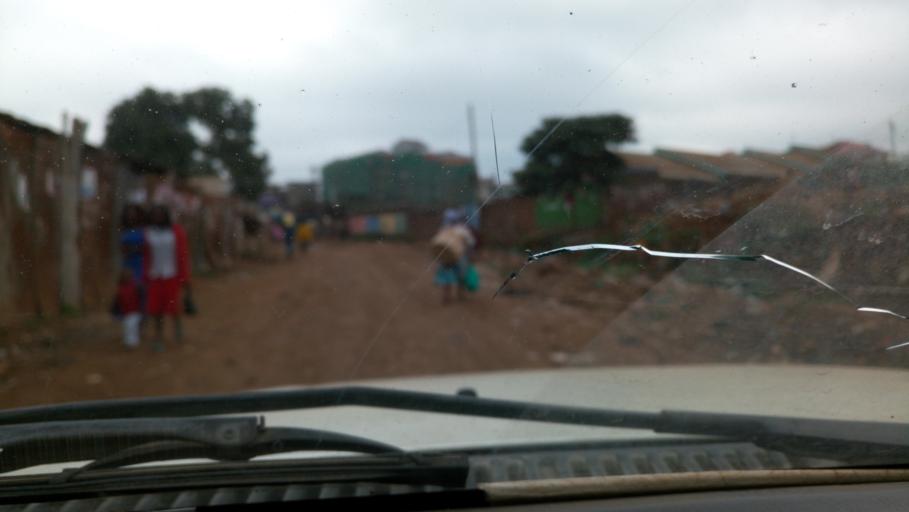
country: KE
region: Nairobi Area
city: Nairobi
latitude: -1.2812
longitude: 36.7431
